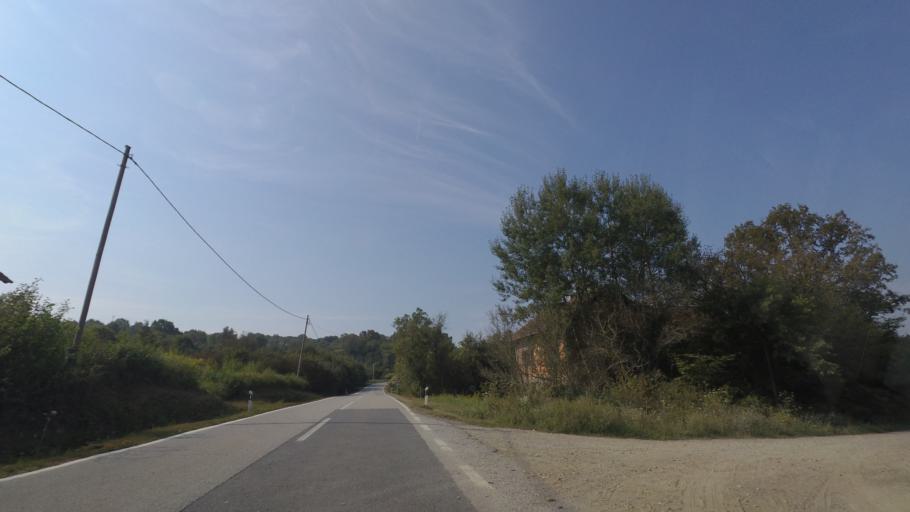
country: HR
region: Sisacko-Moslavacka
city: Novska
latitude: 45.3826
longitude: 17.0285
